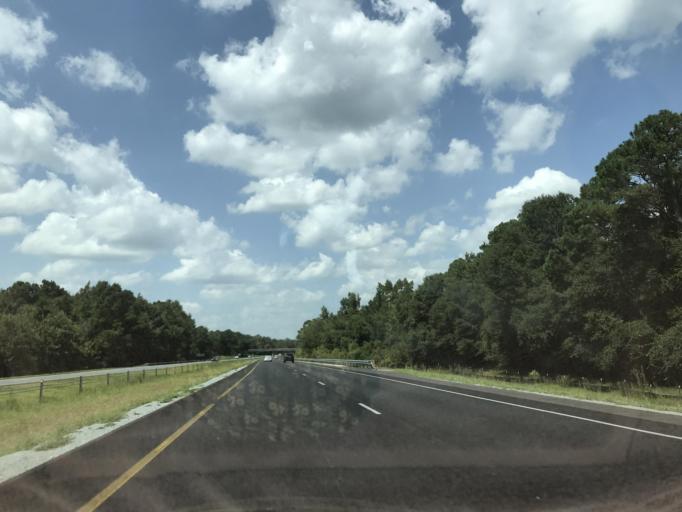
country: US
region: North Carolina
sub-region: Duplin County
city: Warsaw
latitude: 34.9330
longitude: -78.0451
